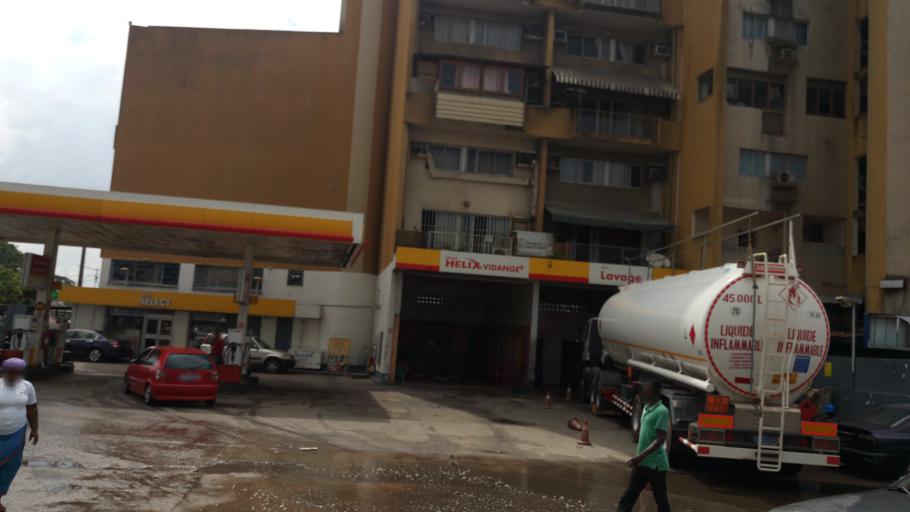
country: CI
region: Lagunes
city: Abidjan
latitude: 5.3092
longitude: -4.0058
